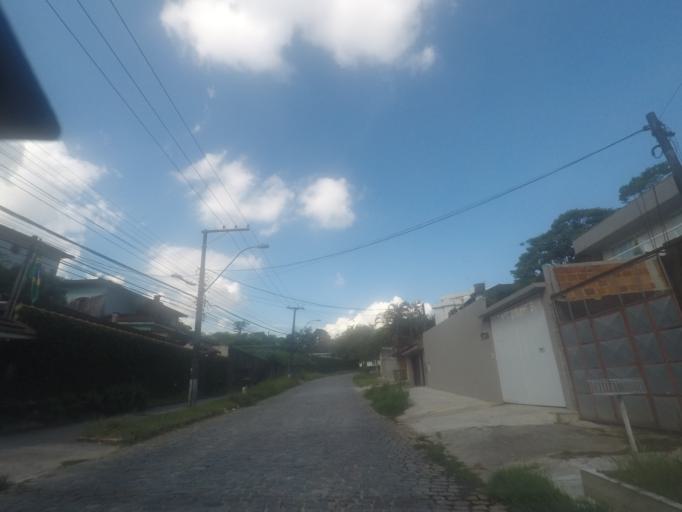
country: BR
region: Rio de Janeiro
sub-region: Petropolis
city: Petropolis
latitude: -22.5218
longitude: -43.2066
